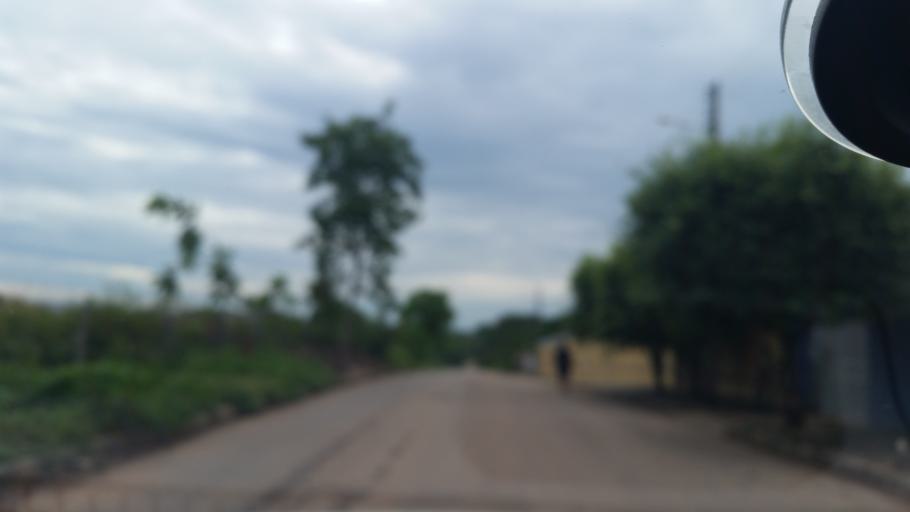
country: BR
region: Goias
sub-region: Uruacu
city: Uruacu
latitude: -14.0173
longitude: -49.1709
